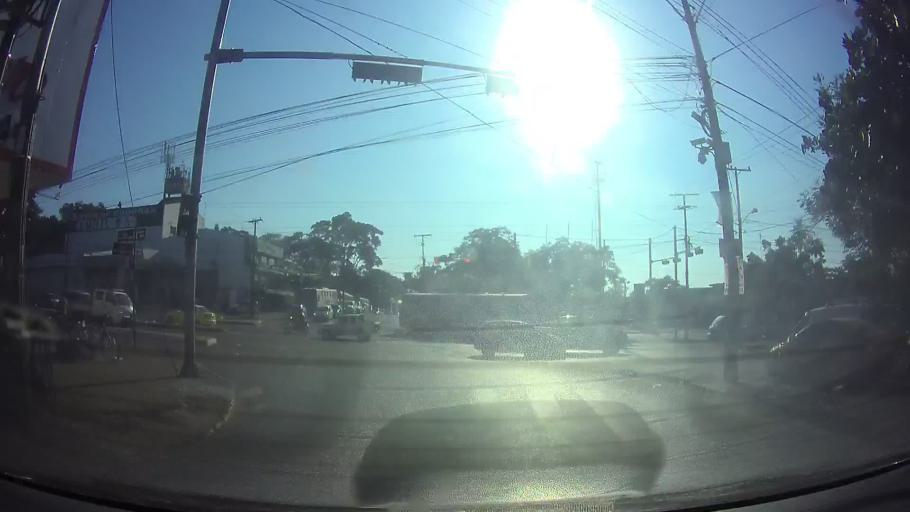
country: PY
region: Central
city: Lambare
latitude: -25.3263
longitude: -57.5975
